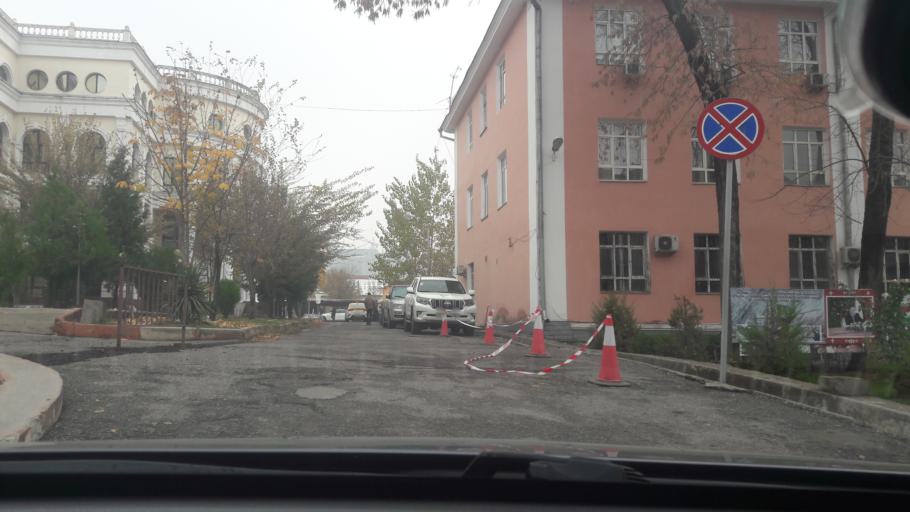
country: TJ
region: Dushanbe
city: Dushanbe
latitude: 38.5754
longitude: 68.7938
